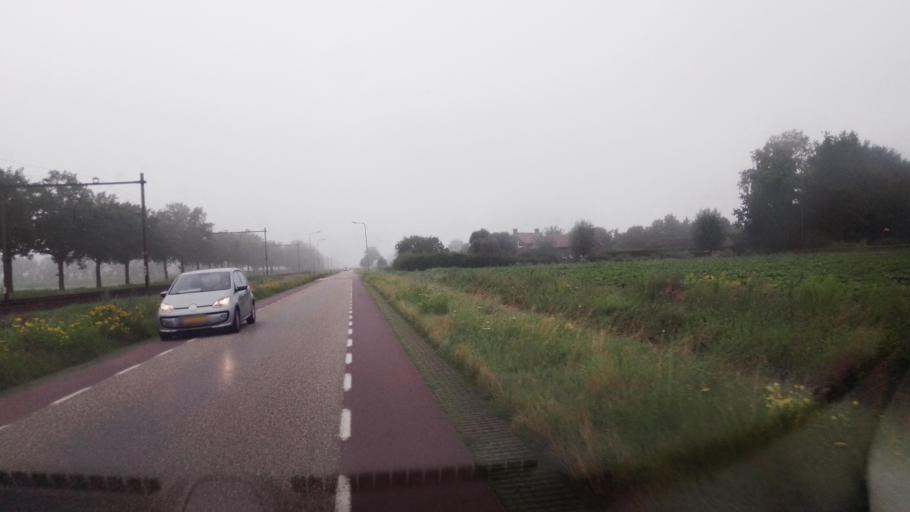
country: NL
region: Limburg
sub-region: Gemeente Peel en Maas
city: Maasbree
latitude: 51.4318
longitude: 6.0196
